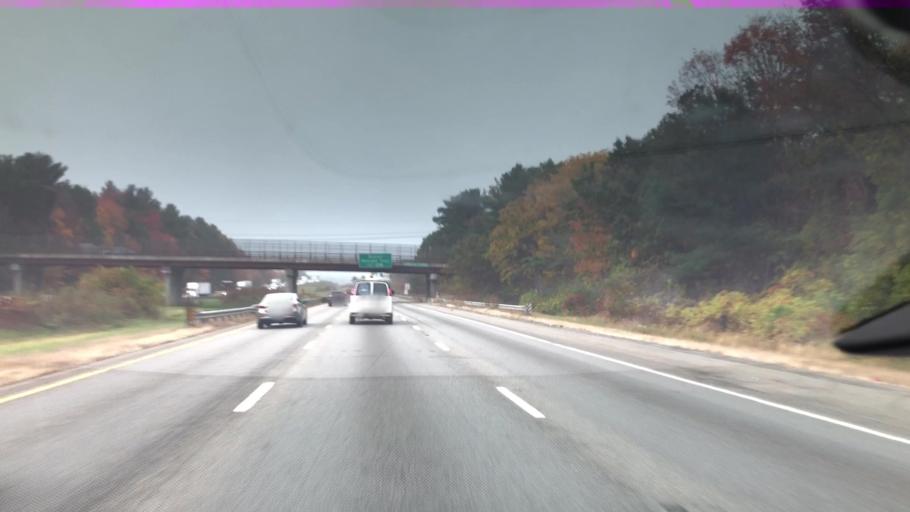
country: US
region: Massachusetts
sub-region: Middlesex County
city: Littleton Common
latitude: 42.5326
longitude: -71.4989
